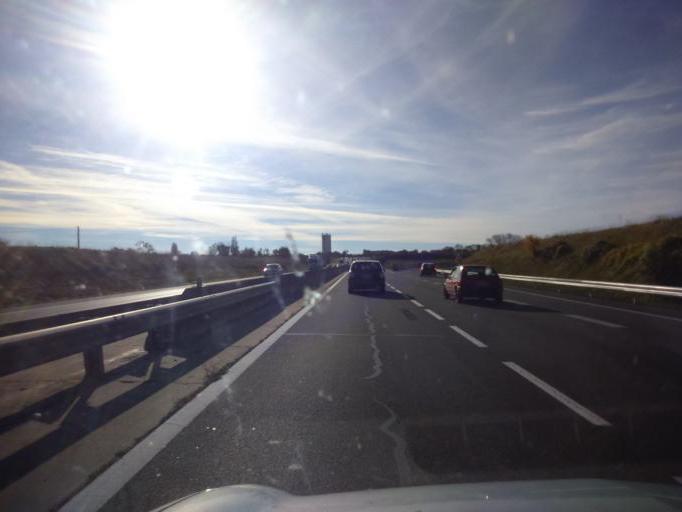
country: FR
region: Poitou-Charentes
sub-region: Departement de la Charente-Maritime
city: Aytre
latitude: 46.1453
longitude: -1.1088
